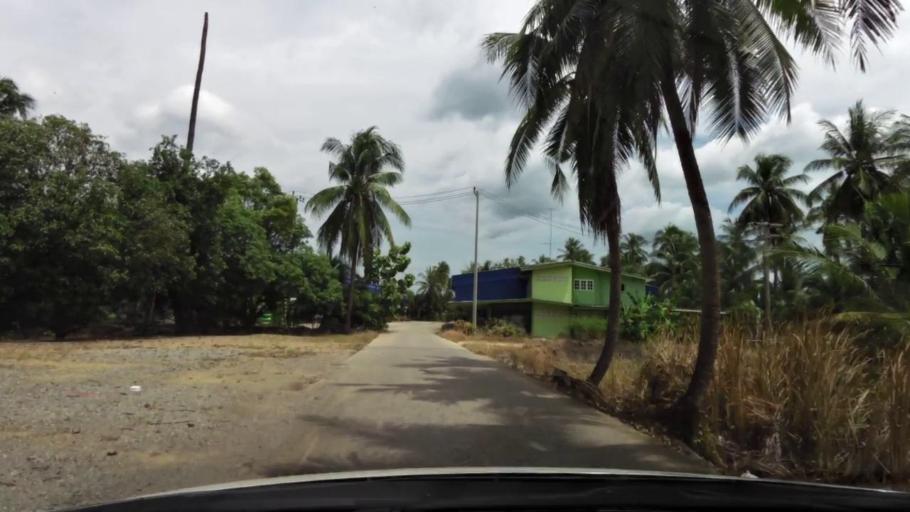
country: TH
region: Ratchaburi
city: Damnoen Saduak
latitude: 13.5200
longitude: 100.0056
